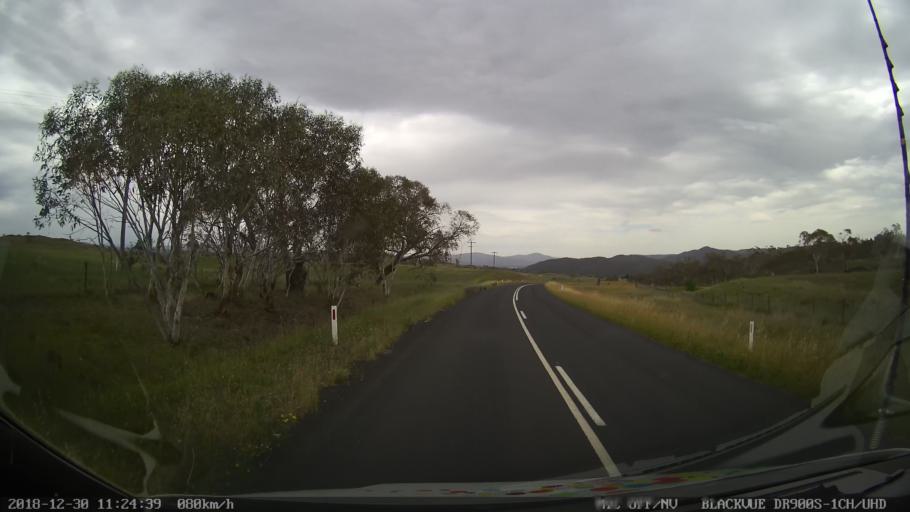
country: AU
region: New South Wales
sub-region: Snowy River
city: Jindabyne
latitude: -36.4813
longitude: 148.6484
